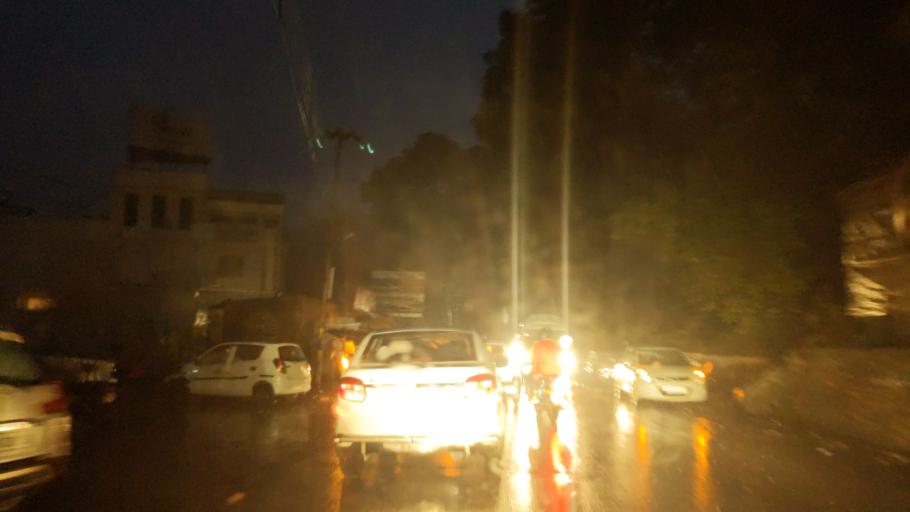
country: IN
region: Uttarakhand
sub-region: Naini Tal
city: Bhim Tal
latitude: 29.2858
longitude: 79.5479
